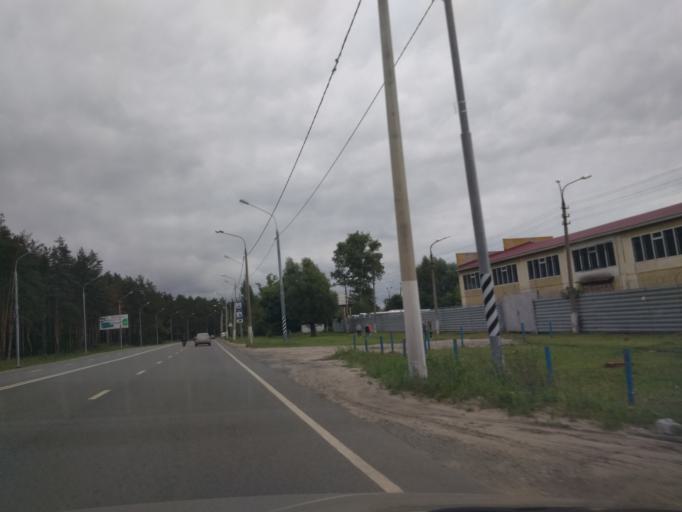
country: RU
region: Moskovskaya
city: Orekhovo-Zuyevo
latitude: 55.8294
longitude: 38.9643
